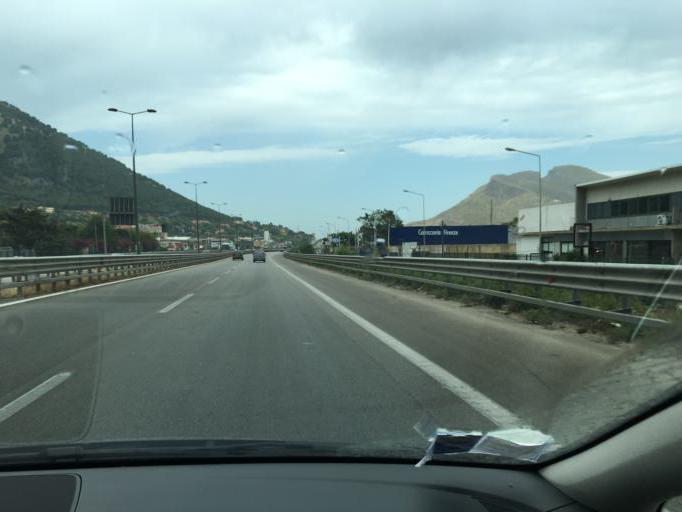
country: IT
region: Sicily
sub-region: Palermo
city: Isola delle Femmine
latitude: 38.1733
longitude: 13.2976
